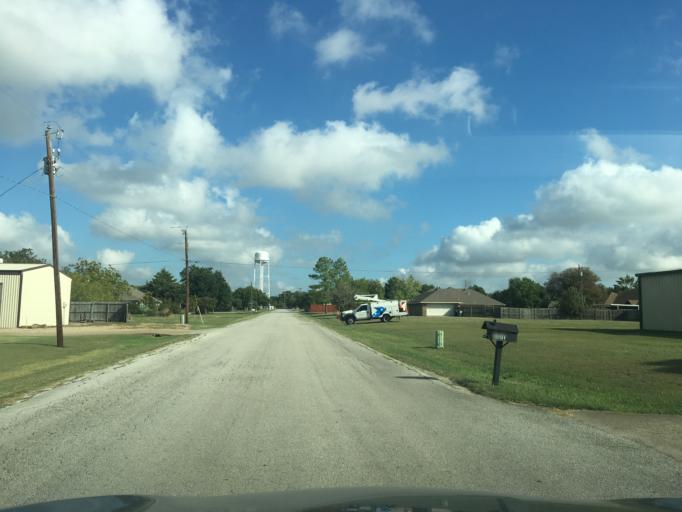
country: US
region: Texas
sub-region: Dallas County
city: Sachse
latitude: 32.9700
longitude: -96.5917
